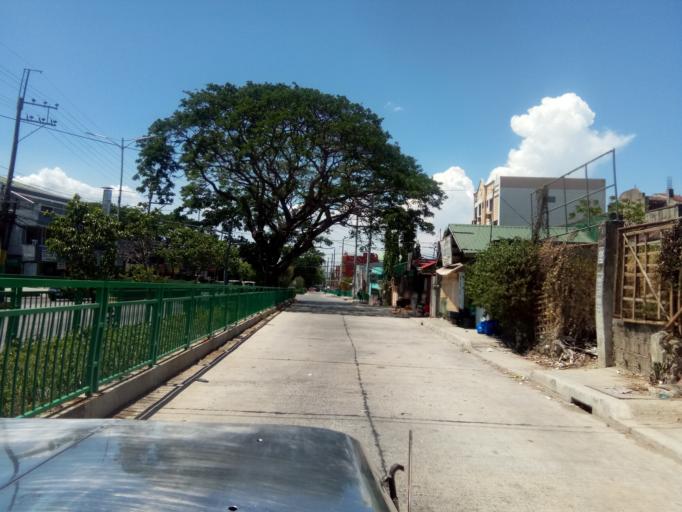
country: PH
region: Calabarzon
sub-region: Province of Cavite
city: Dasmarinas
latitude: 14.3188
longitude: 120.9641
